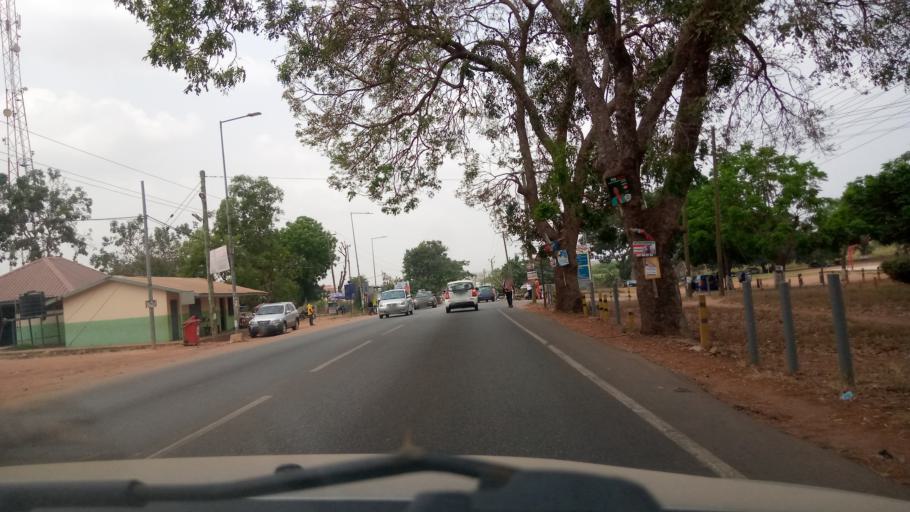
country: GH
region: Greater Accra
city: Dome
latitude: 5.6677
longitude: -0.2314
